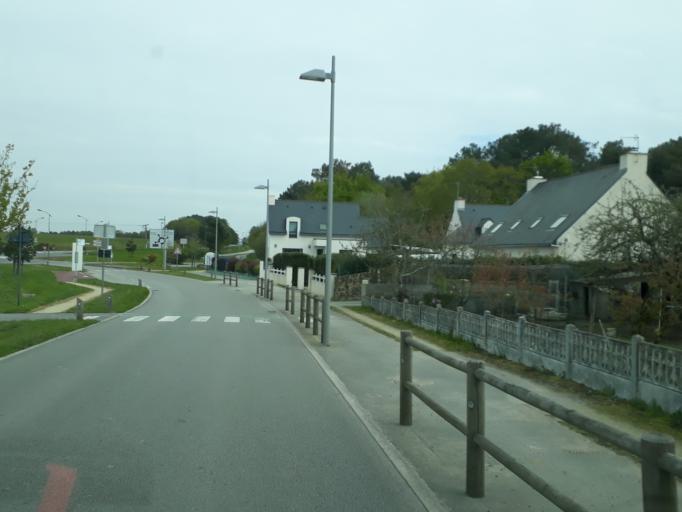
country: FR
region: Brittany
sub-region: Departement du Morbihan
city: Surzur
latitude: 47.5905
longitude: -2.6259
